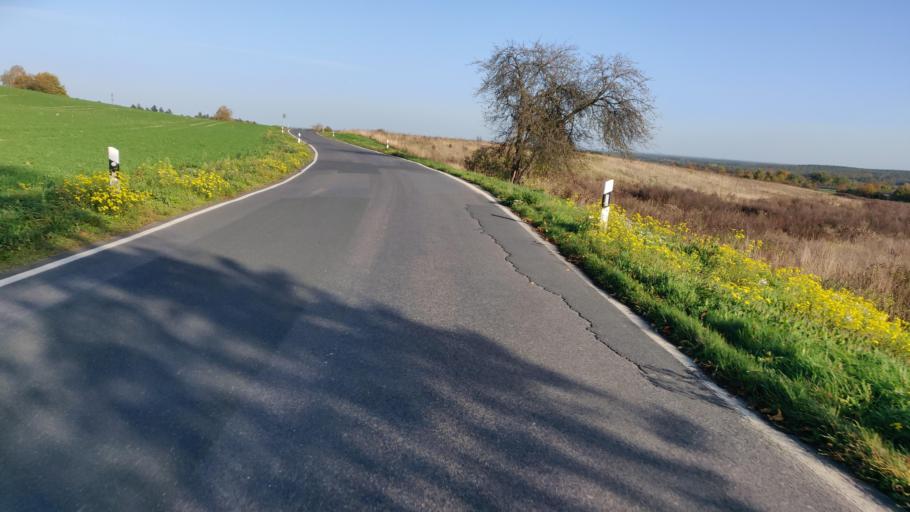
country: DE
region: Brandenburg
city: Grosskmehlen
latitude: 51.3610
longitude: 13.7286
